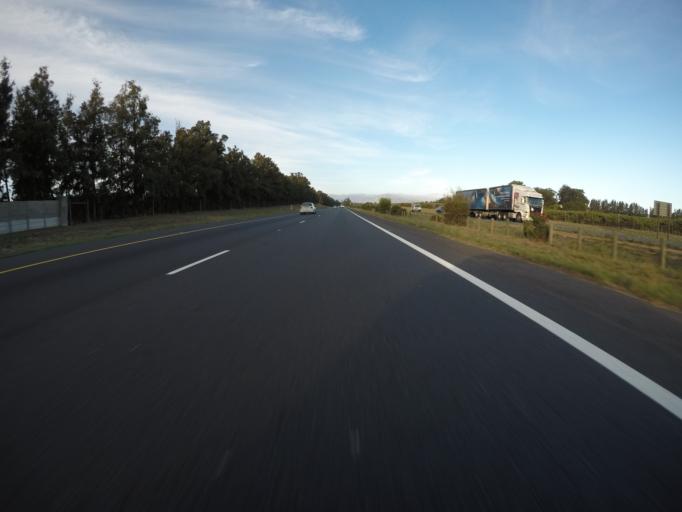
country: ZA
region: Western Cape
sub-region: Cape Winelands District Municipality
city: Stellenbosch
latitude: -33.8013
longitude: 18.8577
